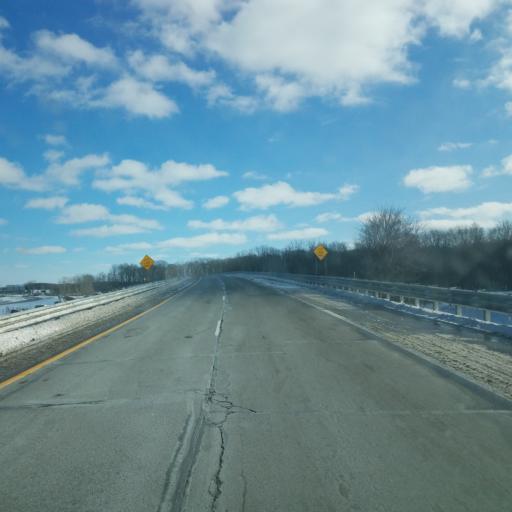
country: US
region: Michigan
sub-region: Ingham County
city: Holt
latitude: 42.6779
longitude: -84.4956
